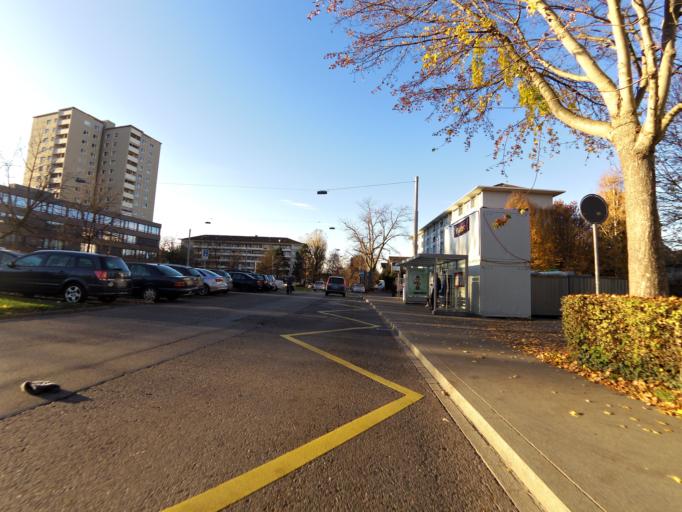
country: CH
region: Zurich
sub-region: Bezirk Zuerich
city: Zuerich (Kreis 3) / Sihlfeld
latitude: 47.3736
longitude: 8.5035
